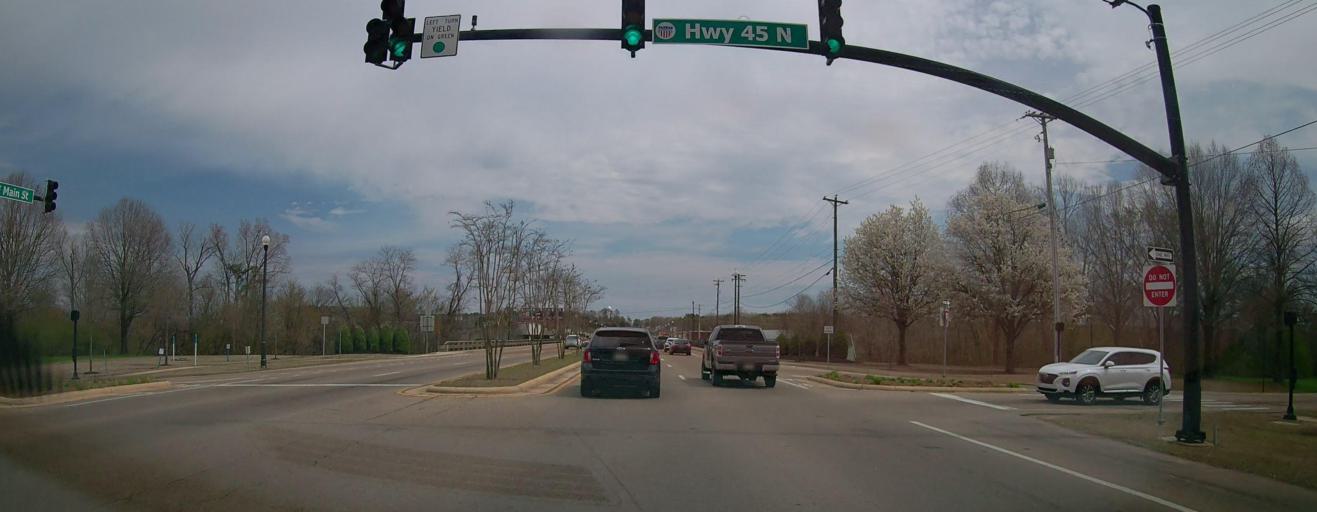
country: US
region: Mississippi
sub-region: Lee County
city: Tupelo
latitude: 34.2576
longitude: -88.6930
